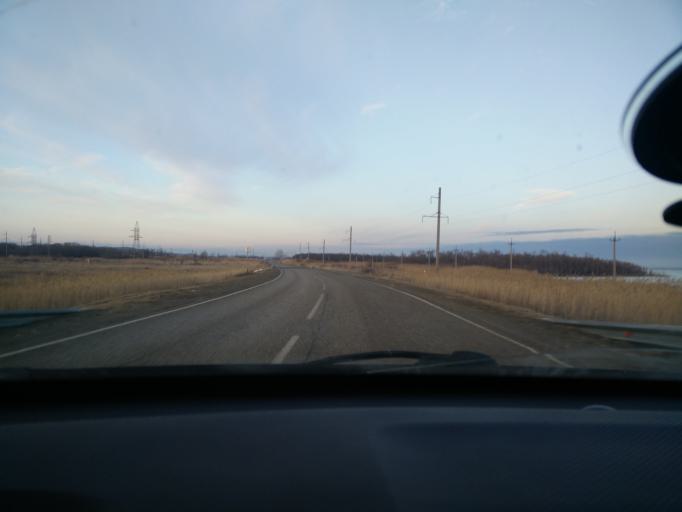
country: RU
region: Stavropol'skiy
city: Tatarka
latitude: 44.9972
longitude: 41.7572
